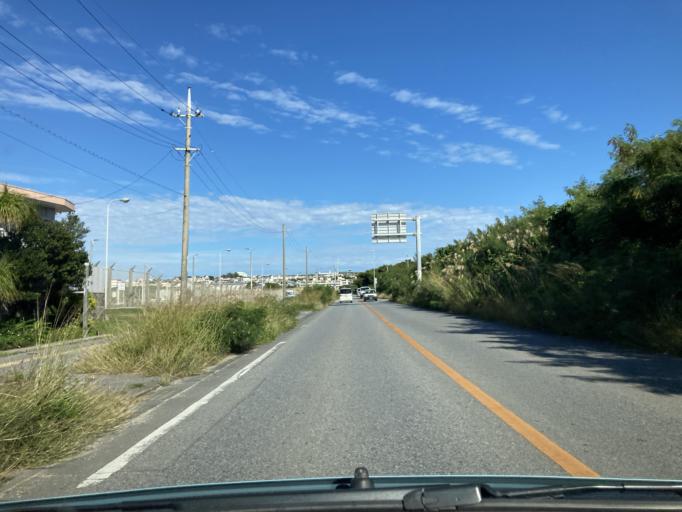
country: JP
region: Okinawa
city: Okinawa
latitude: 26.3732
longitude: 127.7461
